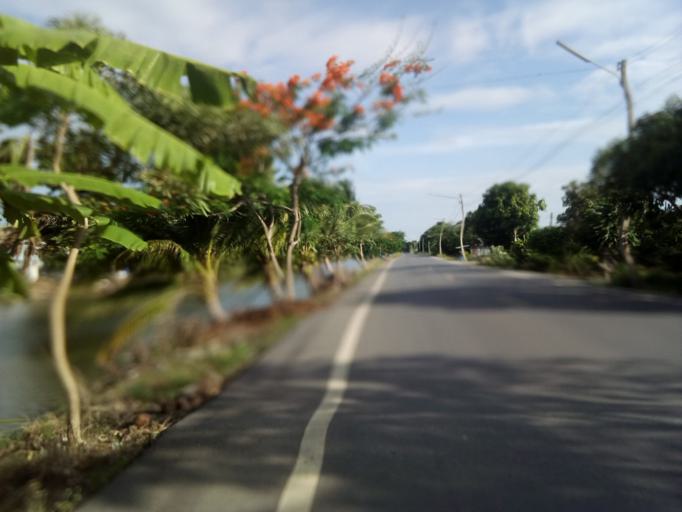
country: TH
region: Pathum Thani
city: Nong Suea
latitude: 14.1037
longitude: 100.8461
